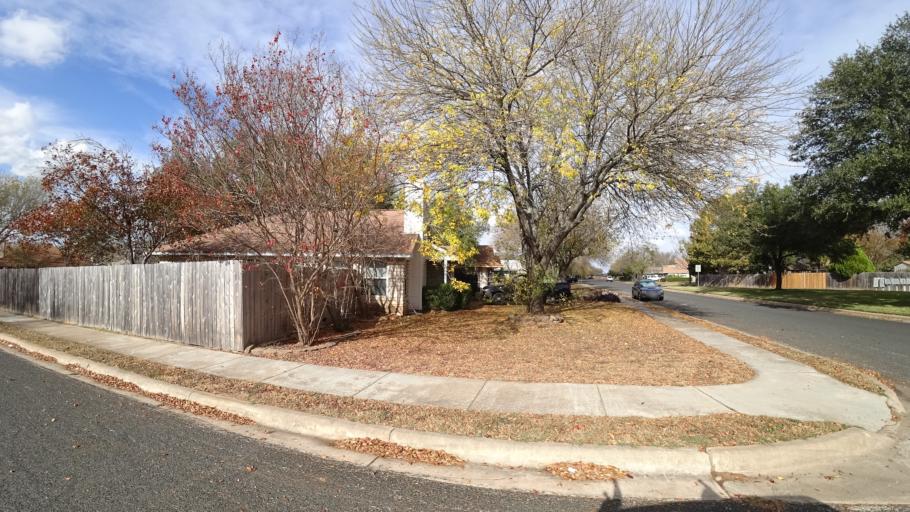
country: US
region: Texas
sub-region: Williamson County
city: Brushy Creek
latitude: 30.5076
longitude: -97.7407
